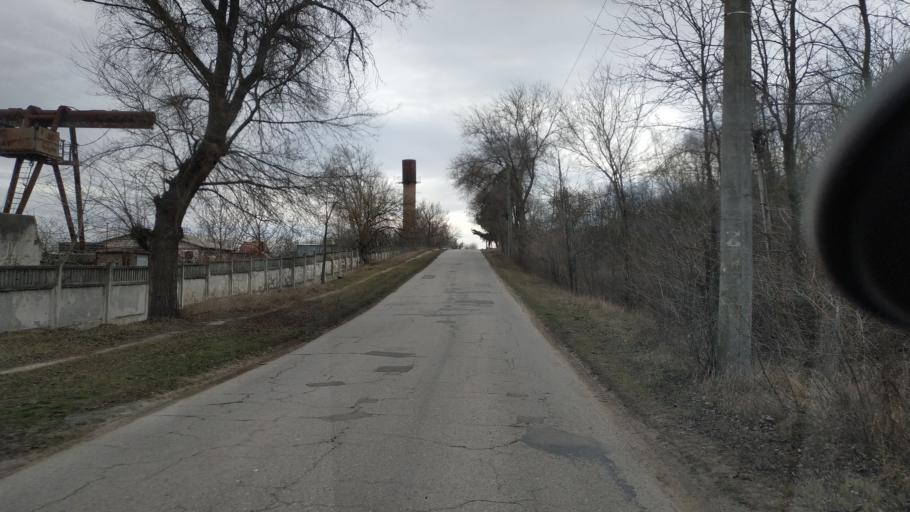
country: MD
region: Chisinau
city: Vadul lui Voda
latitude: 47.1000
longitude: 29.0685
